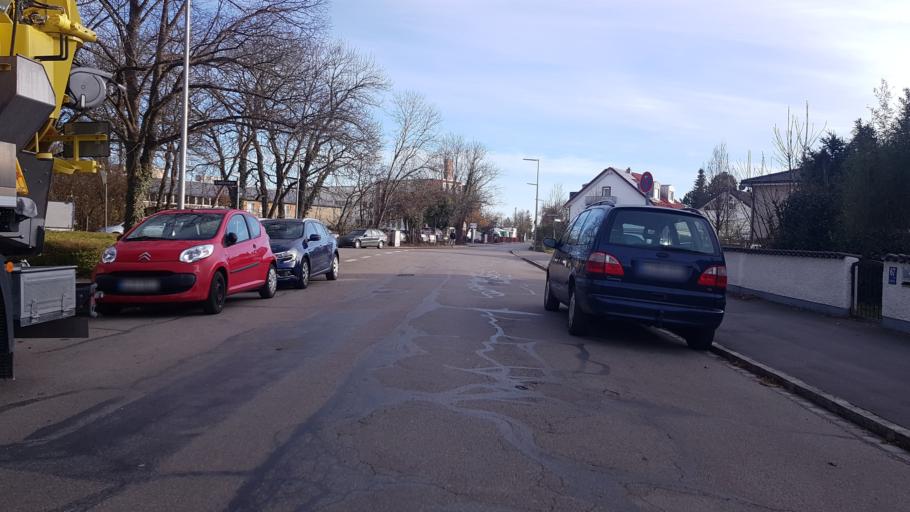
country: DE
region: Bavaria
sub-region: Upper Bavaria
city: Oberschleissheim
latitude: 48.2108
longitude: 11.5385
